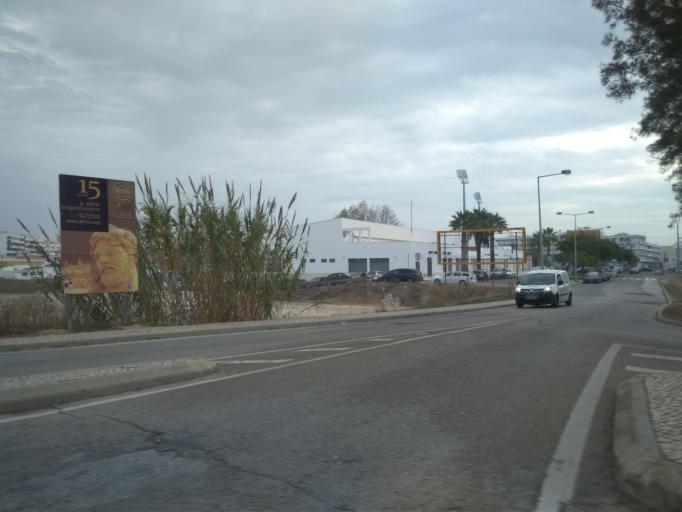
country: PT
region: Faro
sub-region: Olhao
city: Olhao
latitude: 37.0288
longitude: -7.8517
